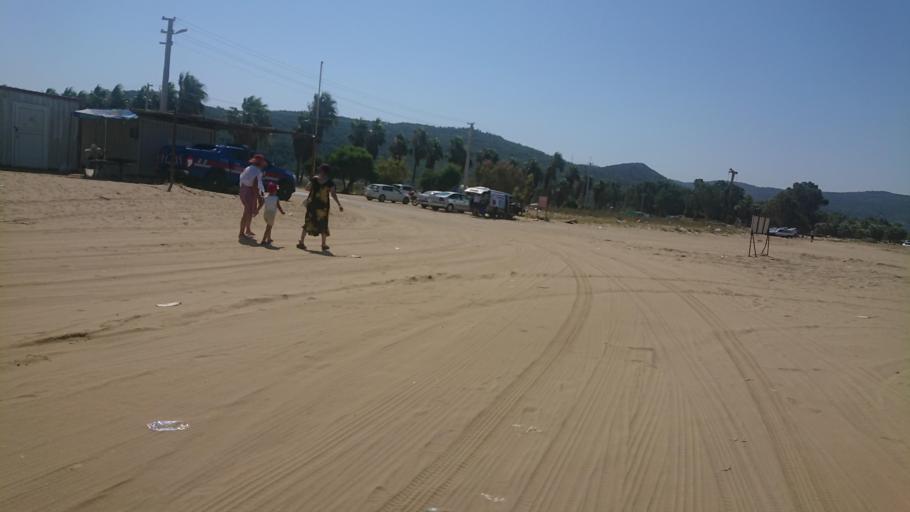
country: TR
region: Aydin
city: Kusadasi
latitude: 37.9438
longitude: 27.2742
